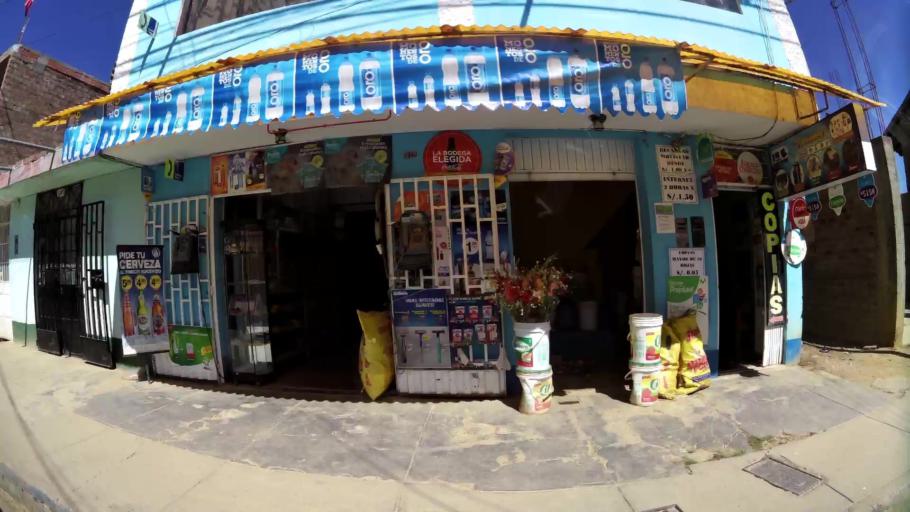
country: PE
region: Junin
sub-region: Provincia de Concepcion
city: Concepcion
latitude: -11.9213
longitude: -75.3121
